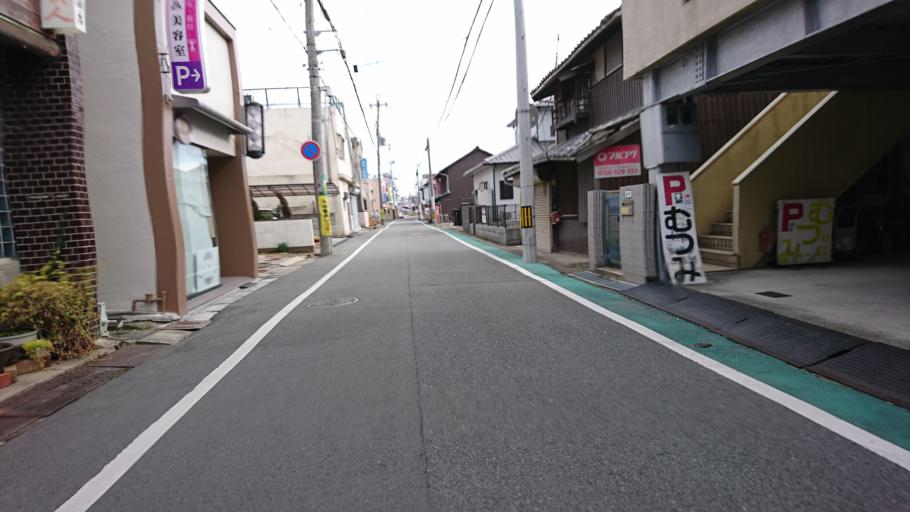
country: JP
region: Hyogo
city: Kakogawacho-honmachi
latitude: 34.7773
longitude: 134.8228
